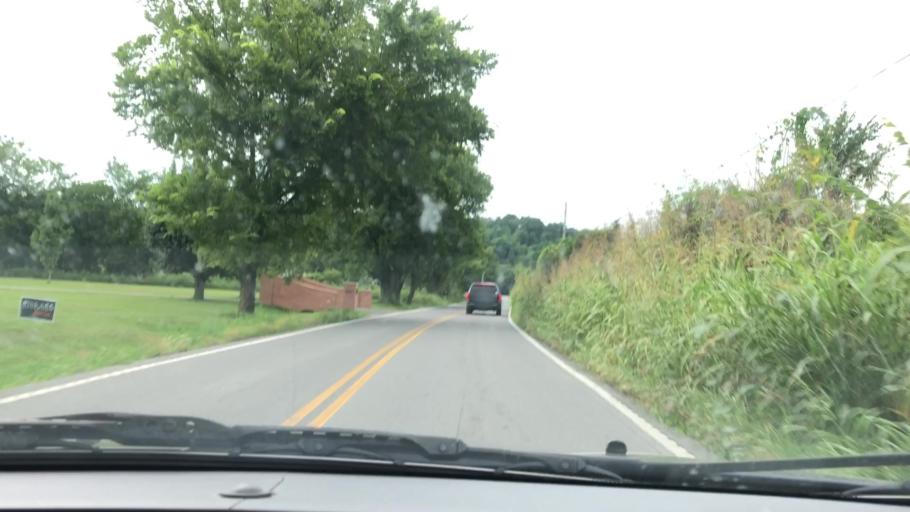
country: US
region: Tennessee
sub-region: Williamson County
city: Thompson's Station
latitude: 35.8045
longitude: -86.9935
